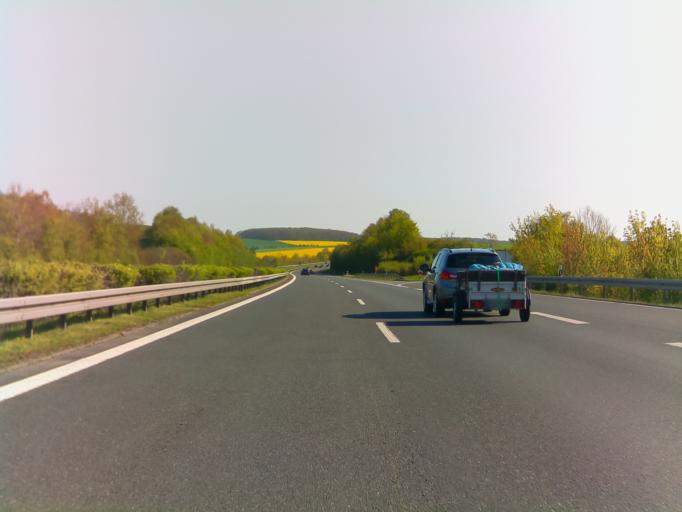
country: DE
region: Baden-Wuerttemberg
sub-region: Regierungsbezirk Stuttgart
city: Grossrinderfeld
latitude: 49.6701
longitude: 9.7703
